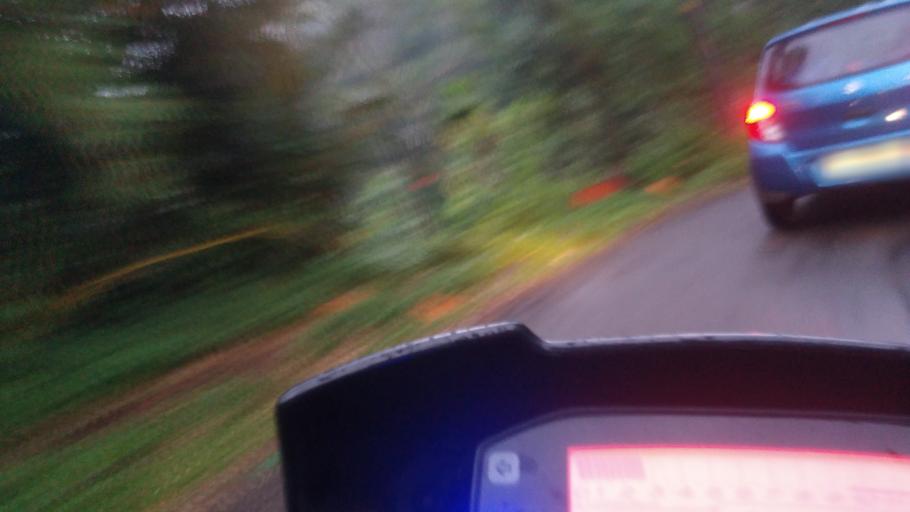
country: IN
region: Kerala
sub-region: Kottayam
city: Erattupetta
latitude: 9.5471
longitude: 76.9731
